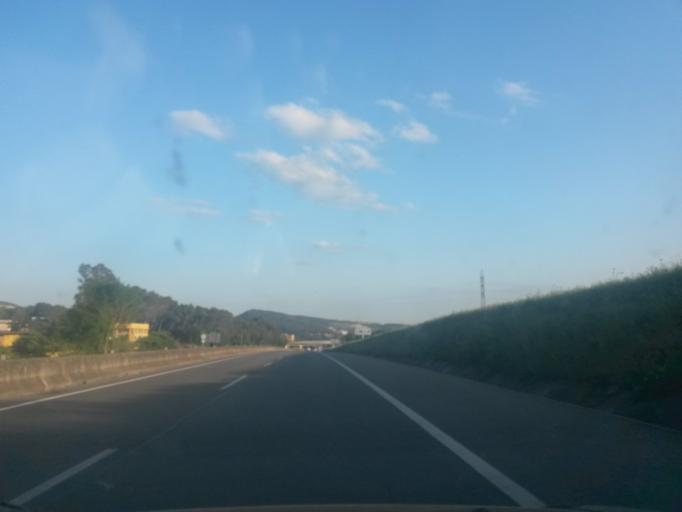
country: ES
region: Catalonia
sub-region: Provincia de Girona
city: Palol de Revardit
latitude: 42.0462
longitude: 2.8196
